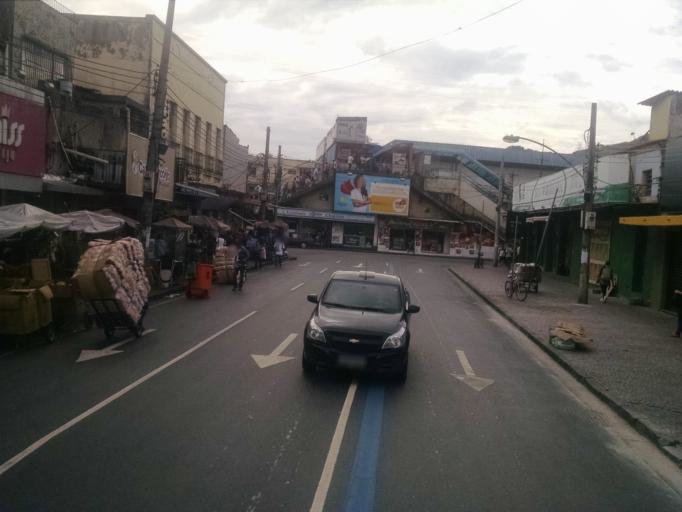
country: BR
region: Rio de Janeiro
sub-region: Sao Joao De Meriti
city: Sao Joao de Meriti
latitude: -22.8762
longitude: -43.3388
